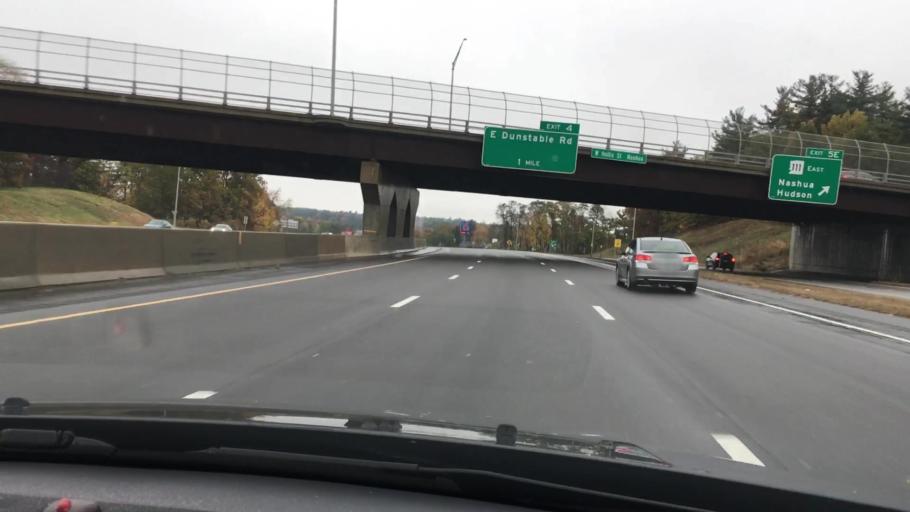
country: US
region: New Hampshire
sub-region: Hillsborough County
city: Nashua
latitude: 42.7473
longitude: -71.4928
